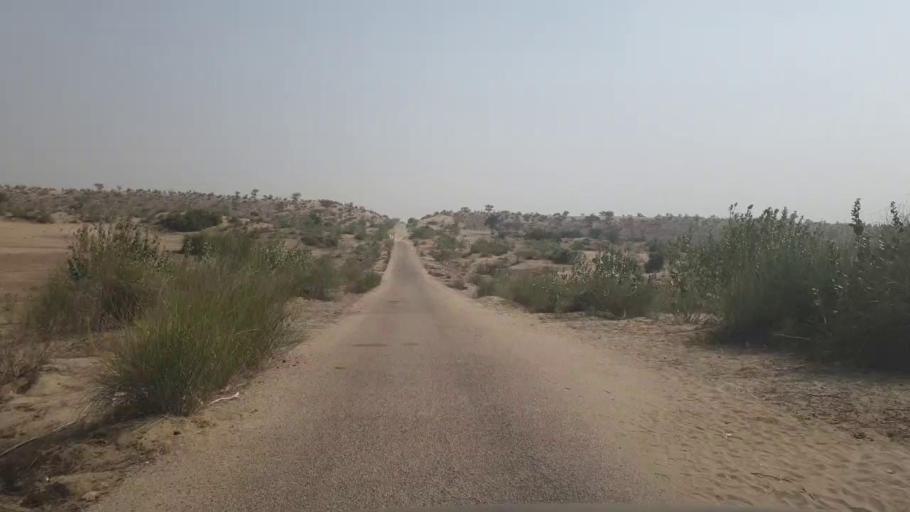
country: PK
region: Sindh
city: Chor
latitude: 25.5937
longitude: 70.0038
